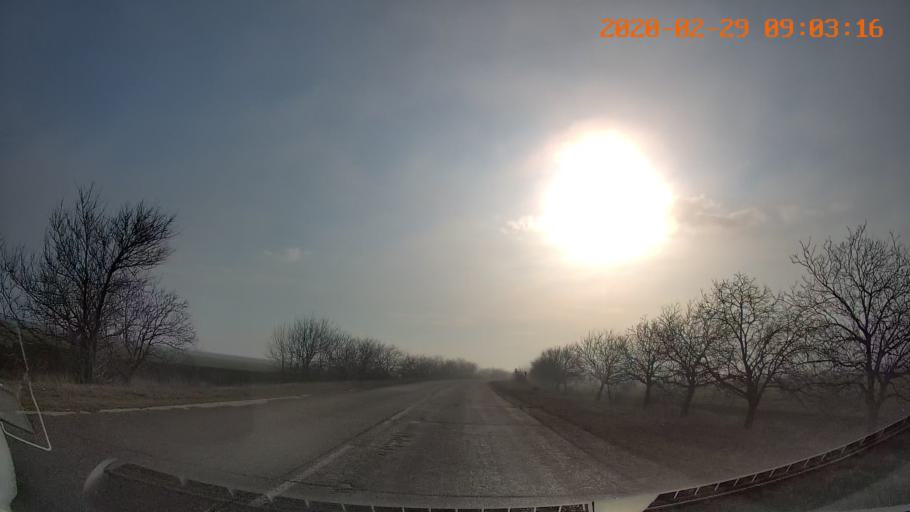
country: UA
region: Odessa
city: Velykoploske
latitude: 46.9170
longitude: 29.7255
